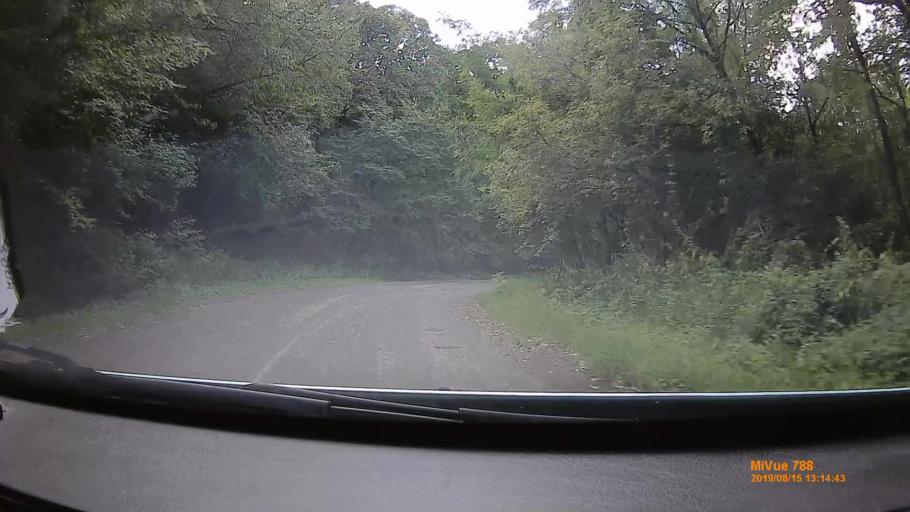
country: HU
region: Borsod-Abauj-Zemplen
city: Sajobabony
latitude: 48.1550
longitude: 20.6752
